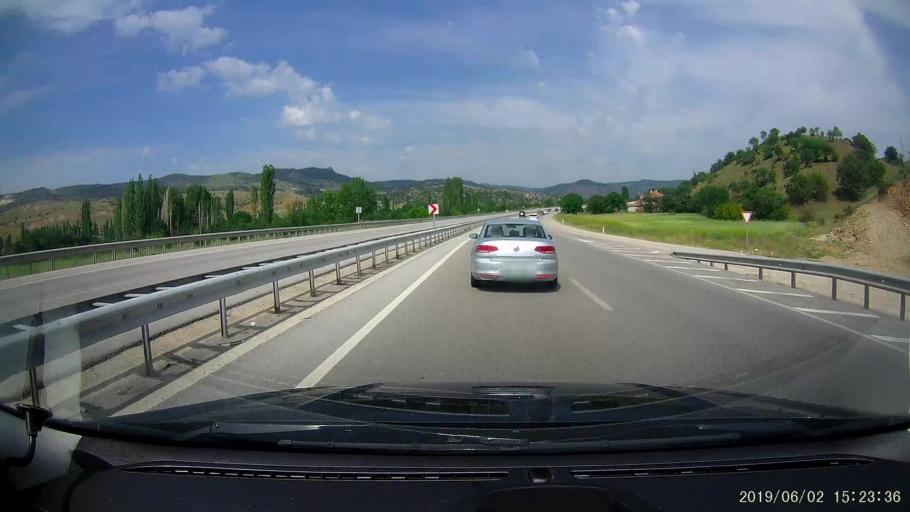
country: TR
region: Amasya
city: Saraycik
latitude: 40.9920
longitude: 34.9838
